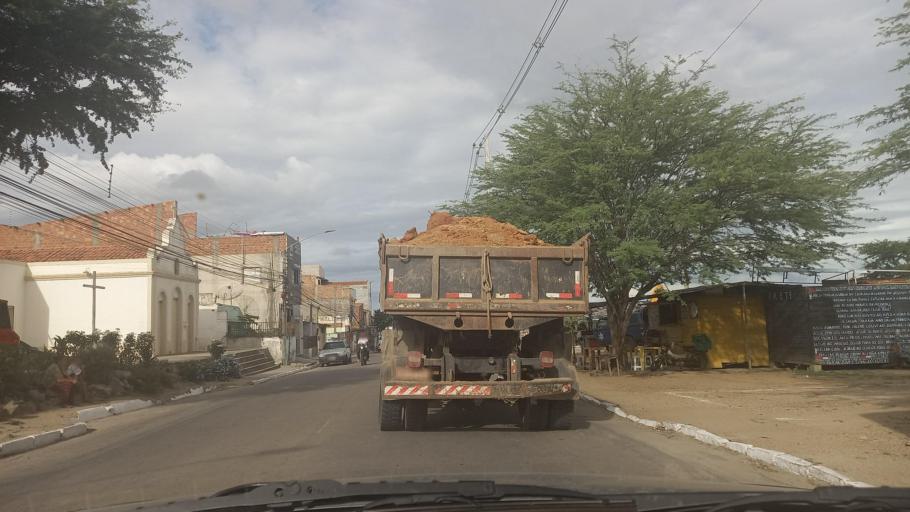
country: BR
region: Pernambuco
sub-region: Caruaru
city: Caruaru
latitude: -8.2859
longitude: -35.9984
